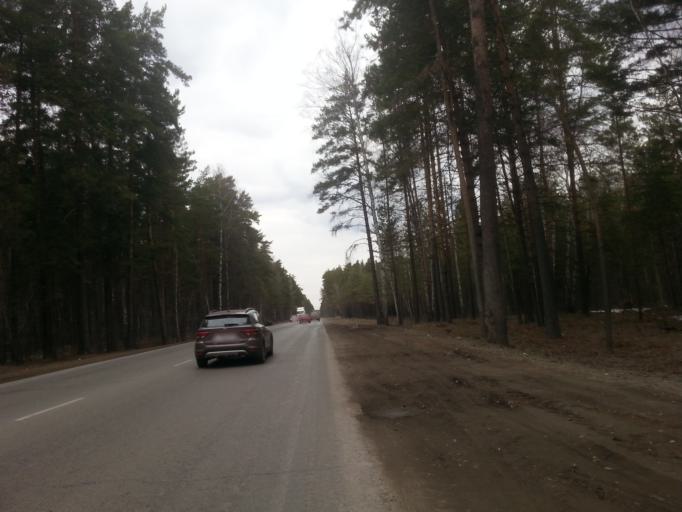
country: RU
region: Altai Krai
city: Yuzhnyy
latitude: 53.2729
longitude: 83.7228
